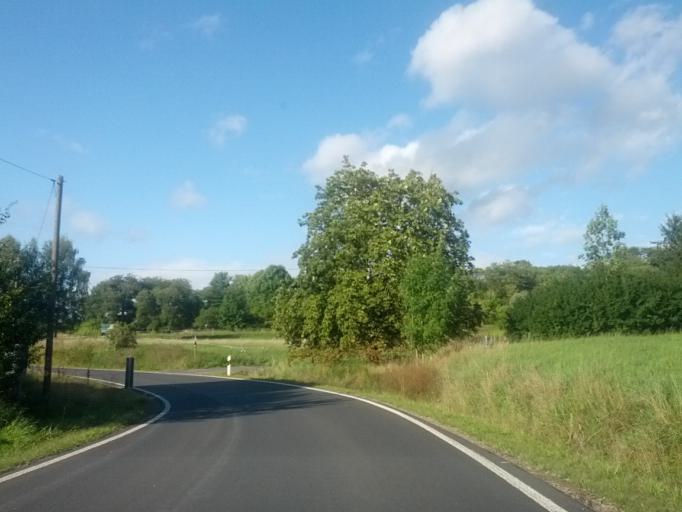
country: DE
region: Thuringia
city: Lauchroden
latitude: 50.9868
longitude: 10.1591
